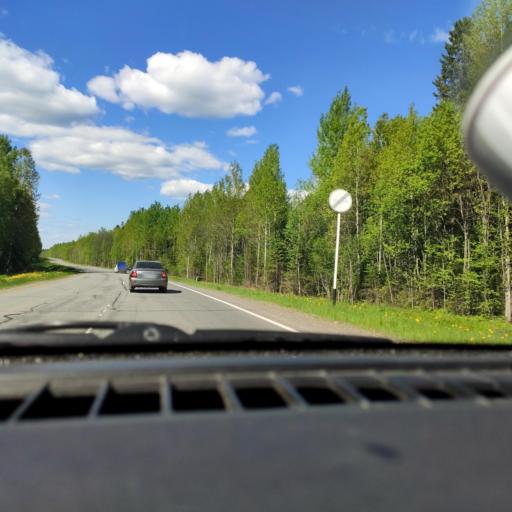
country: RU
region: Perm
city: Polazna
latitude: 58.2634
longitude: 56.1680
